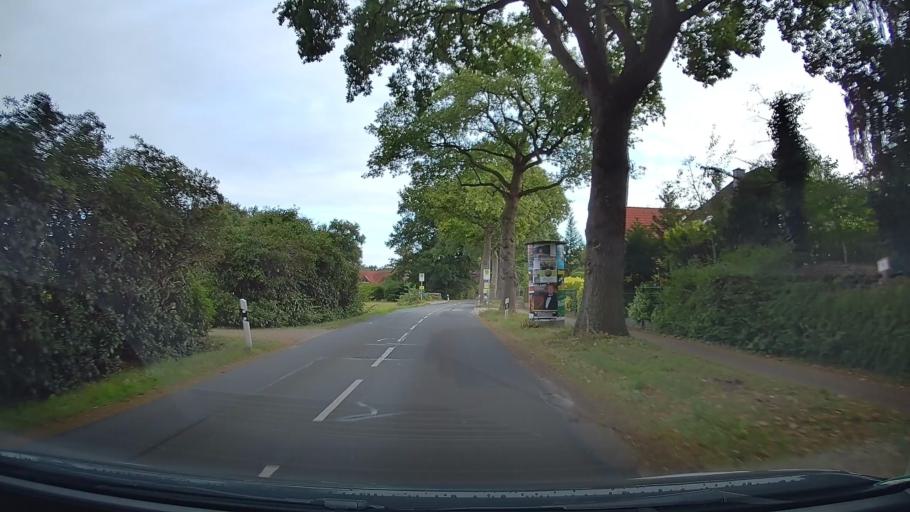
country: DE
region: Lower Saxony
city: Oldenburg
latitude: 53.1326
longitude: 8.1443
